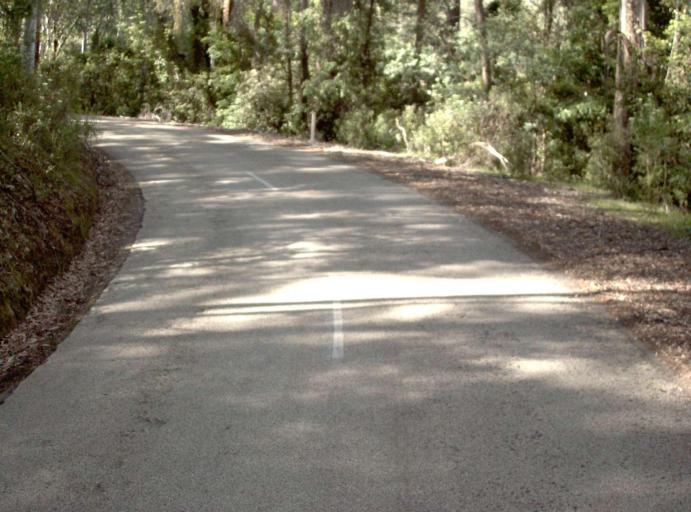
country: AU
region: Victoria
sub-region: East Gippsland
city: Lakes Entrance
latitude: -37.4401
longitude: 148.5899
